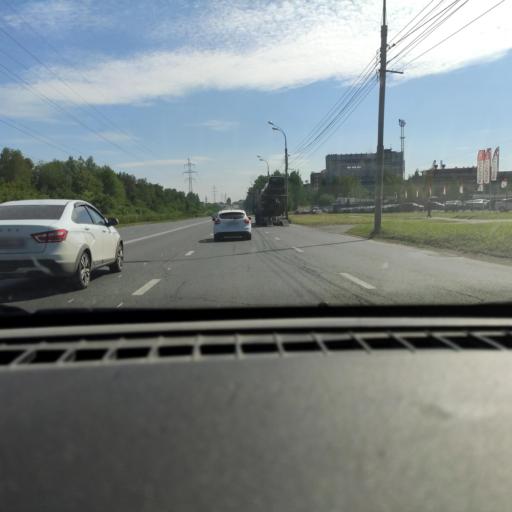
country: RU
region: Udmurtiya
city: Khokhryaki
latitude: 56.8962
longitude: 53.2917
